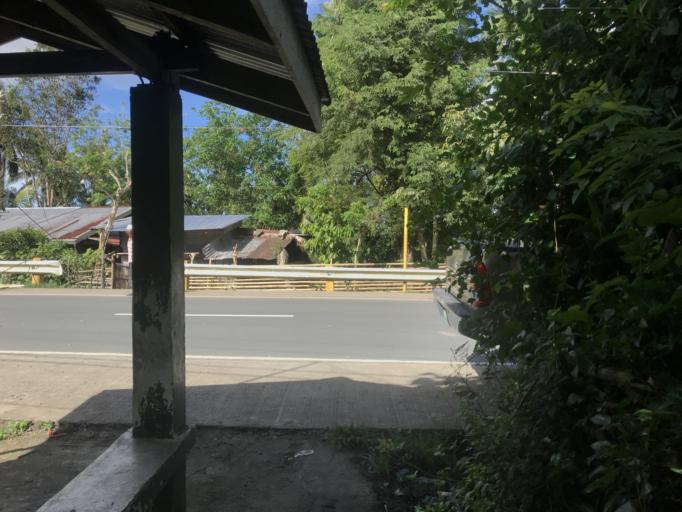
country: PH
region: Calabarzon
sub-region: Province of Quezon
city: Macalelon
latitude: 13.7827
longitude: 122.1401
